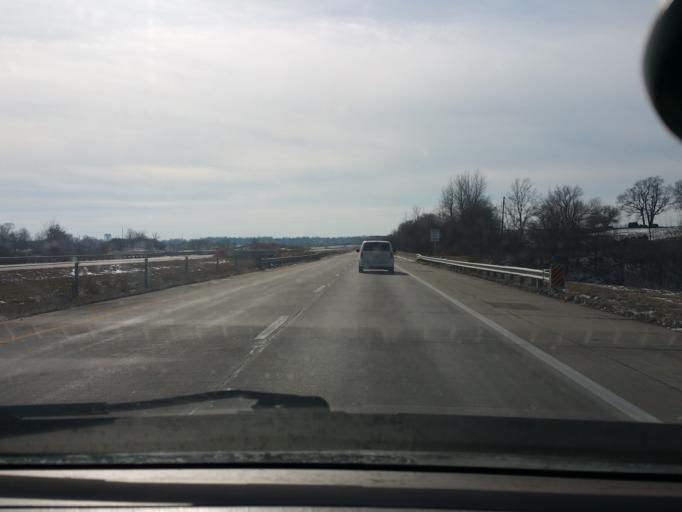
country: US
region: Missouri
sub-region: Clay County
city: Liberty
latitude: 39.2874
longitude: -94.4157
